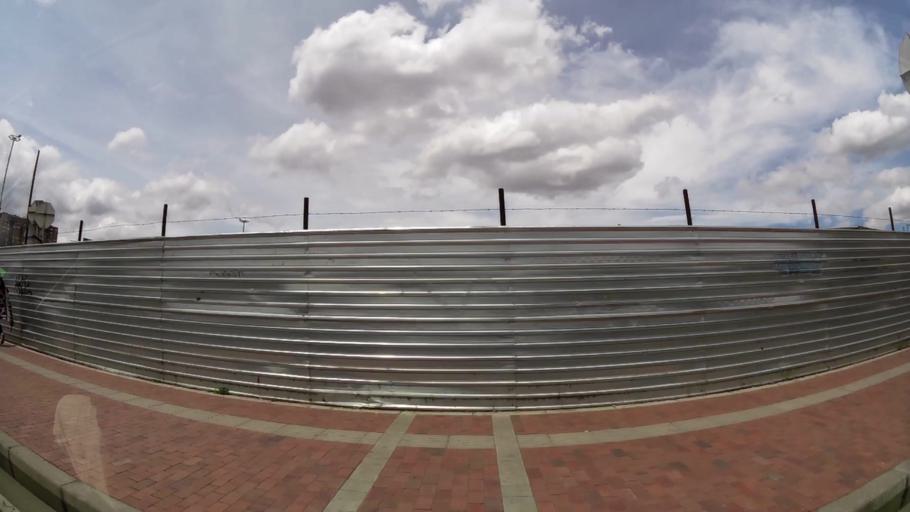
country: CO
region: Bogota D.C.
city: Bogota
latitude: 4.6524
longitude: -74.1454
